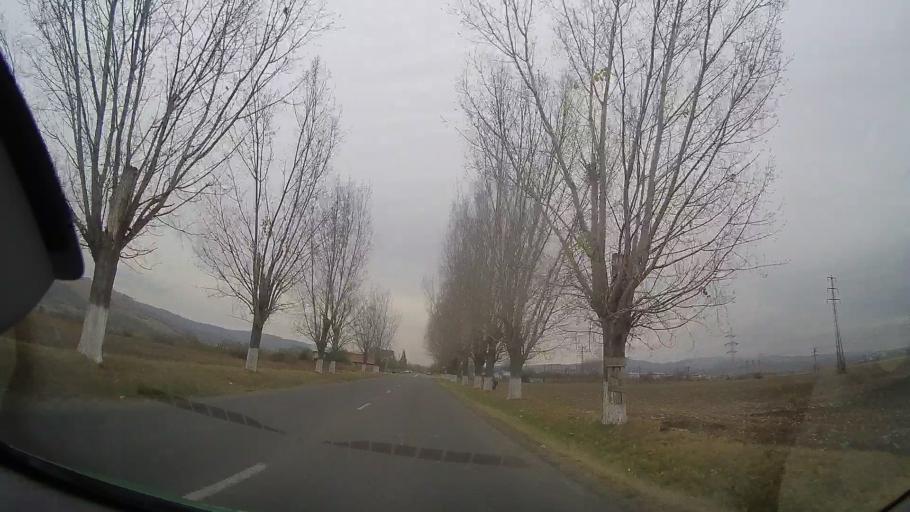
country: RO
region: Prahova
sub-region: Oras Urlati
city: Urlati
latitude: 44.9702
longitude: 26.2338
